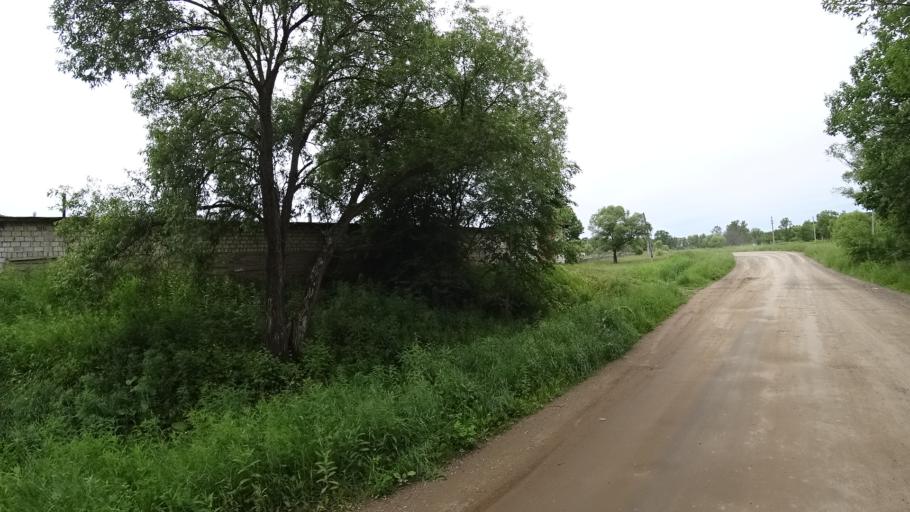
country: RU
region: Primorskiy
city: Novosysoyevka
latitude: 44.2020
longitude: 133.3163
